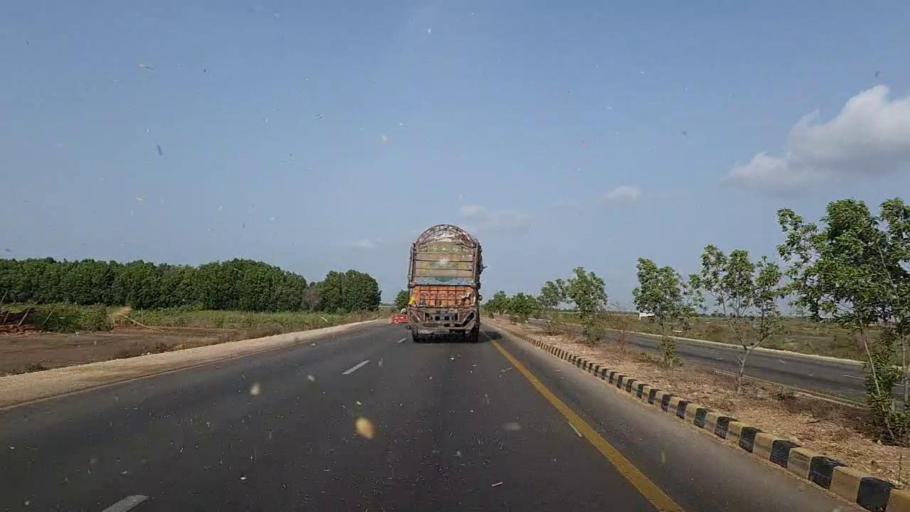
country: PK
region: Sindh
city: Gharo
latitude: 24.7377
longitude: 67.7238
